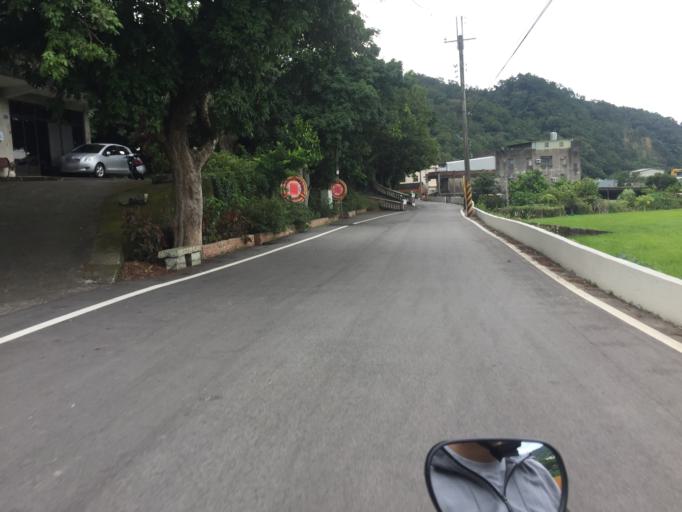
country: TW
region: Taiwan
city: Daxi
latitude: 24.7893
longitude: 121.1677
